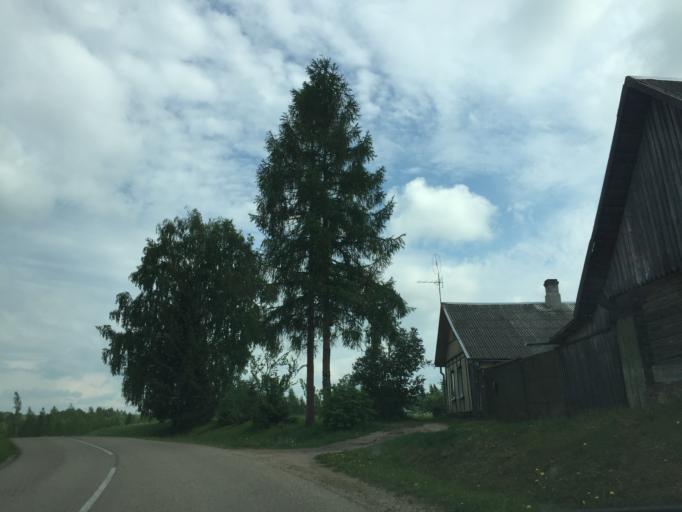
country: LV
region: Dagda
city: Dagda
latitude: 56.2860
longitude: 27.4535
